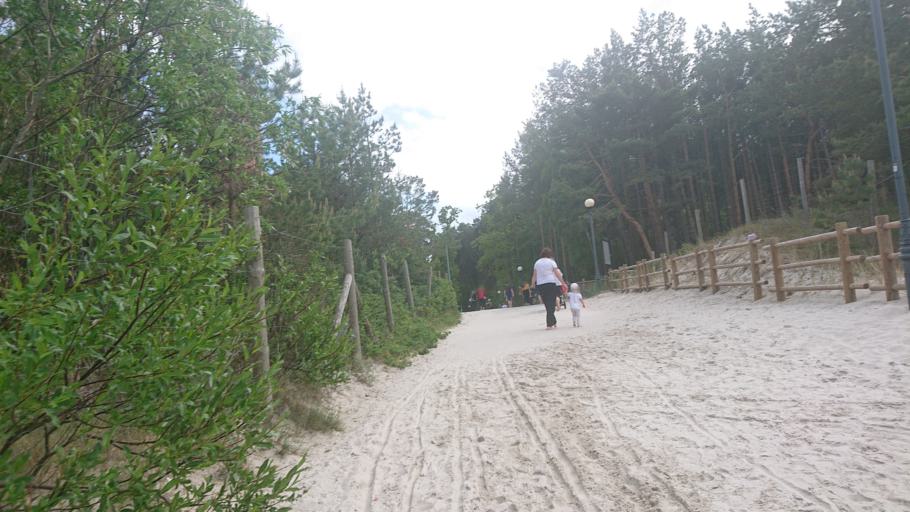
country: PL
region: Pomeranian Voivodeship
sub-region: Powiat pucki
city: Krokowa
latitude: 54.8328
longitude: 18.0882
